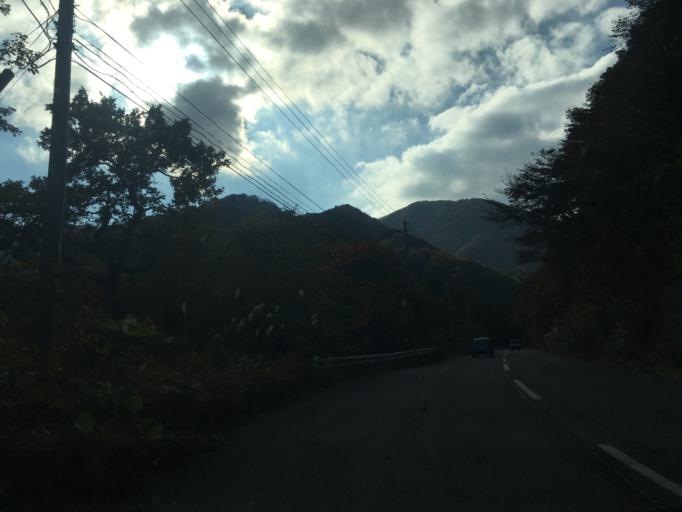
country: JP
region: Fukushima
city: Sukagawa
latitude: 37.2673
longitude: 140.1386
